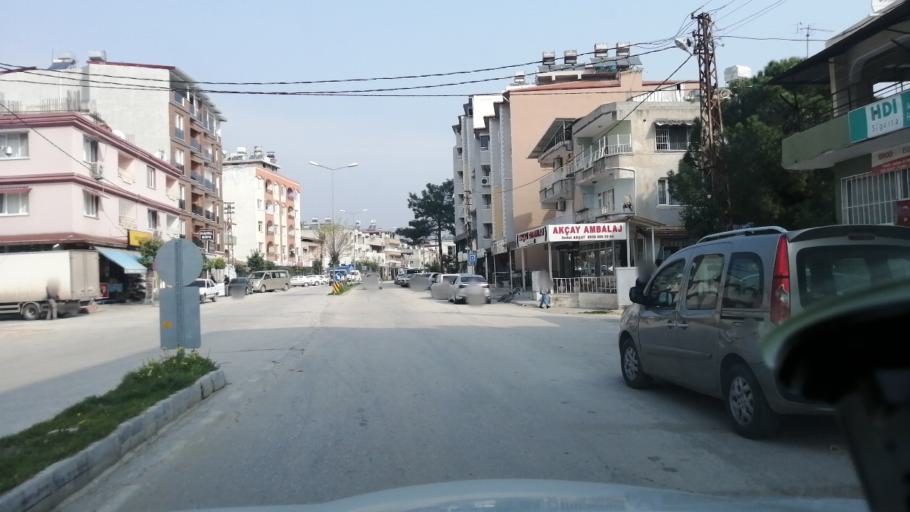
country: TR
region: Hatay
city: Serinyol
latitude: 36.3588
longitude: 36.2100
